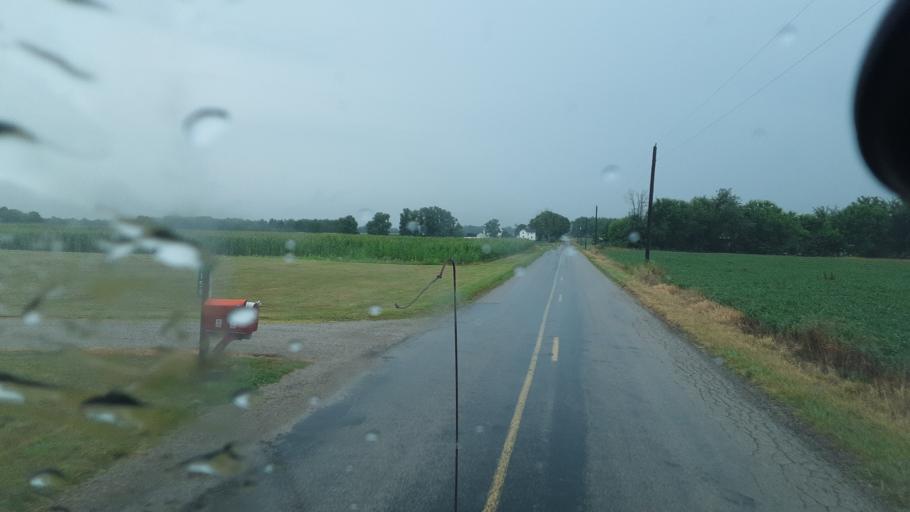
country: US
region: Ohio
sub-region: Williams County
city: Edgerton
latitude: 41.4933
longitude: -84.8148
